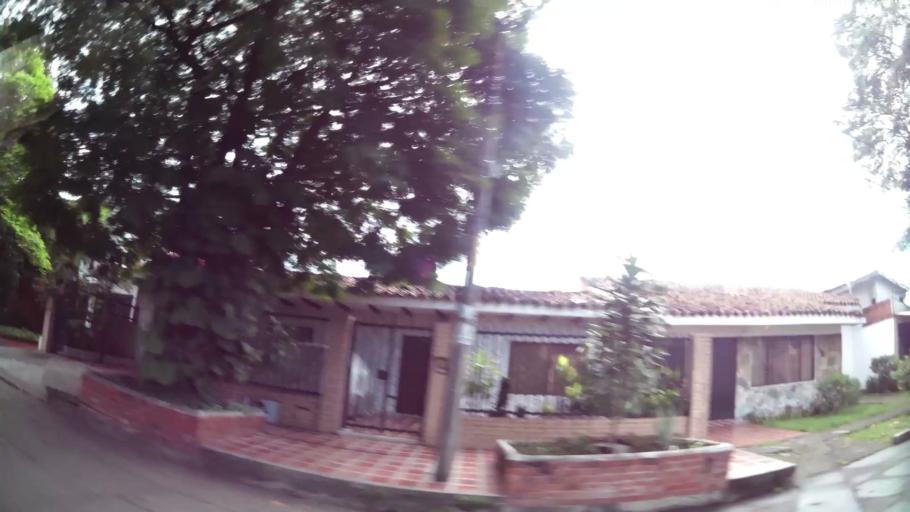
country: CO
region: Valle del Cauca
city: Cali
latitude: 3.4767
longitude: -76.5220
